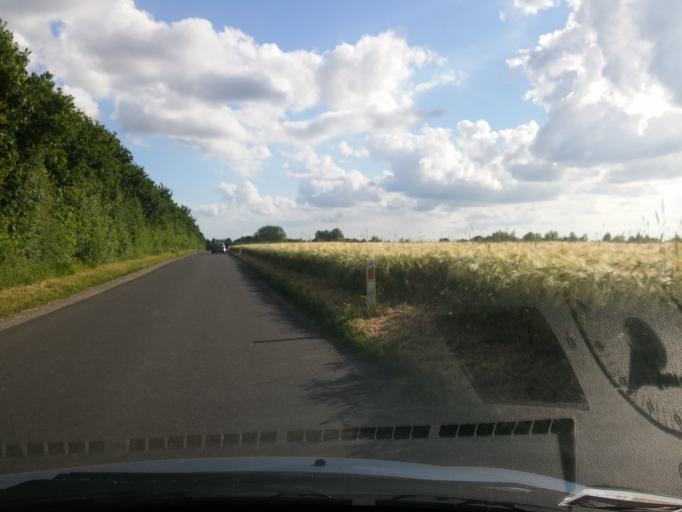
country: DK
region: South Denmark
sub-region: Kerteminde Kommune
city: Langeskov
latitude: 55.3866
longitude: 10.5701
